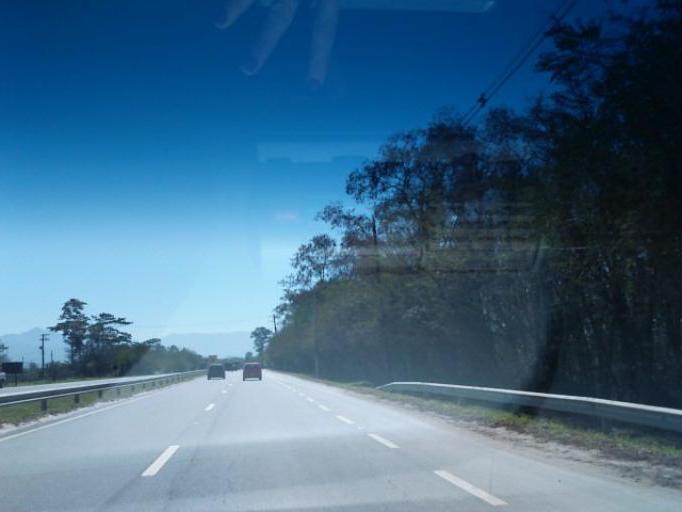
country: BR
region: Sao Paulo
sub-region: Taubate
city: Taubate
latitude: -23.0099
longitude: -45.6407
